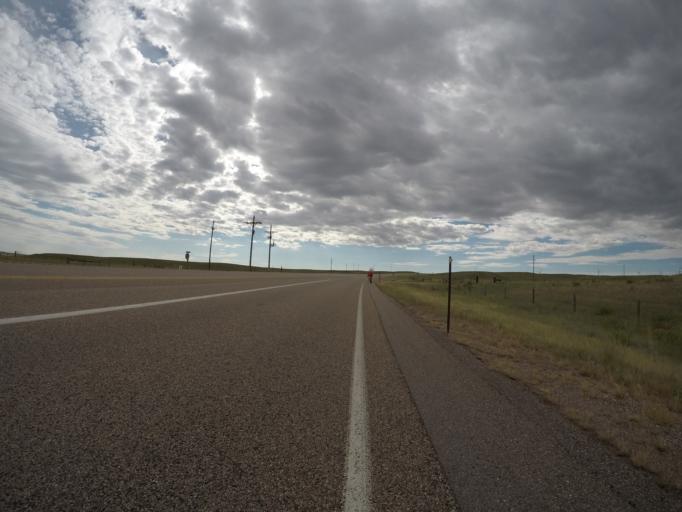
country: US
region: Wyoming
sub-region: Laramie County
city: Cheyenne
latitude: 41.1564
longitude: -105.0401
